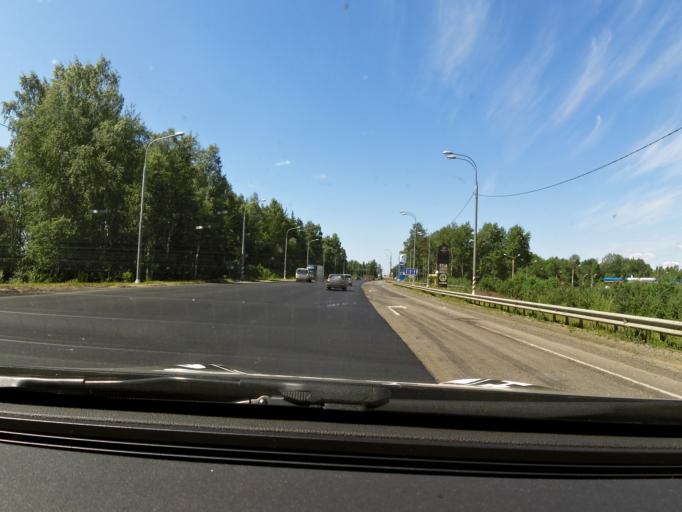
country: RU
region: Novgorod
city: Valday
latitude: 57.9548
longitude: 33.2578
